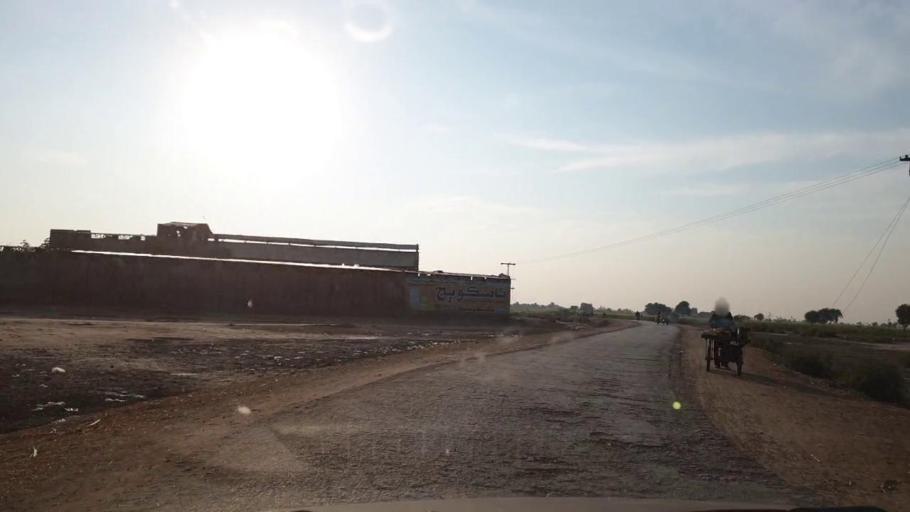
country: PK
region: Sindh
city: Khadro
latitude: 26.1540
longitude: 68.7270
